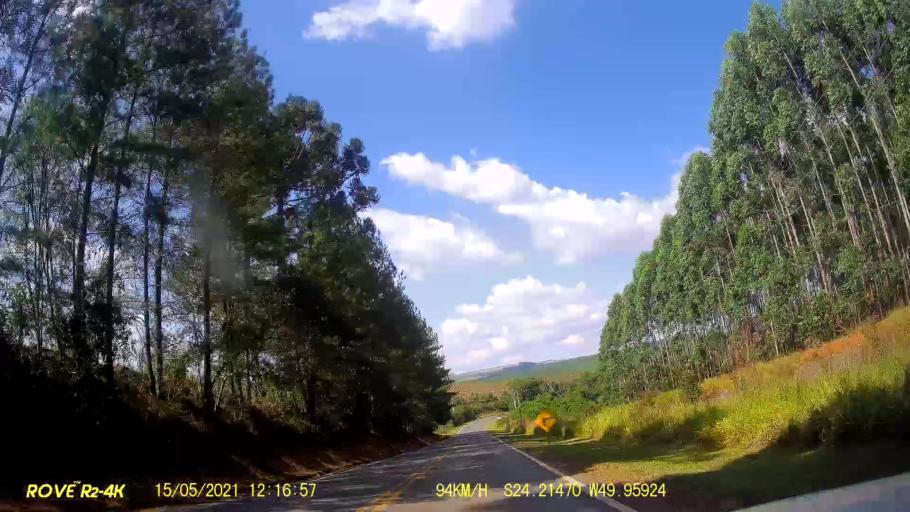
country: BR
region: Parana
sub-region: Jaguariaiva
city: Jaguariaiva
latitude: -24.2146
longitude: -49.9593
